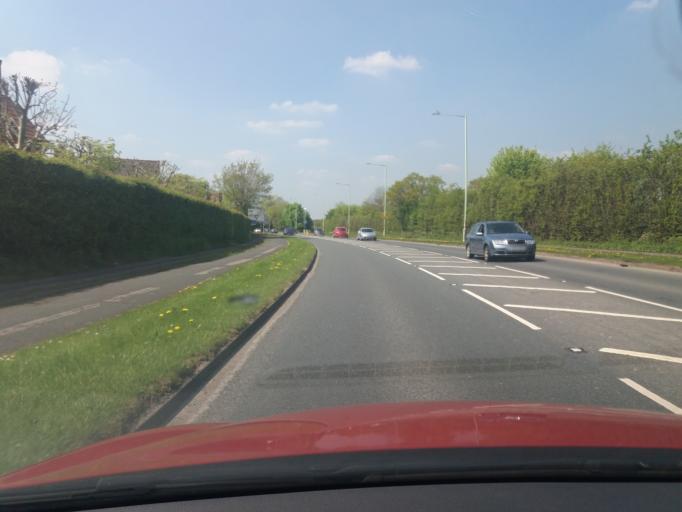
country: GB
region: England
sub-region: Lancashire
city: Euxton
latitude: 53.6691
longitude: -2.6458
